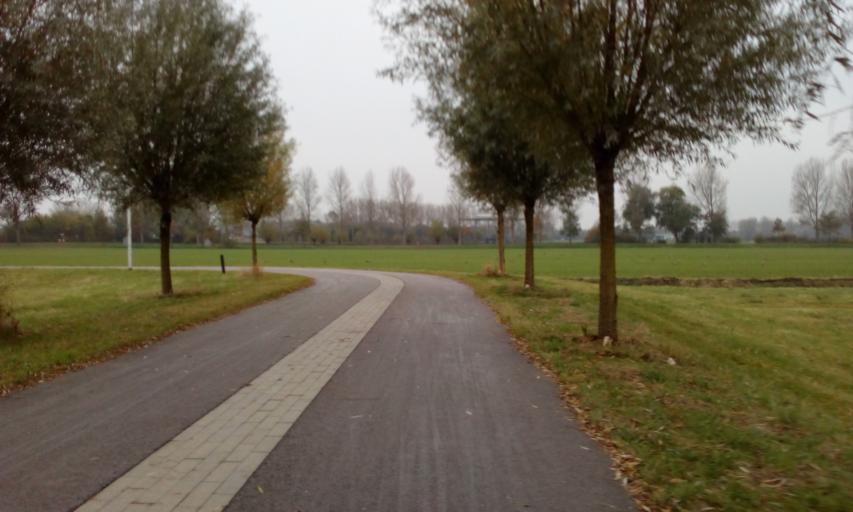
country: NL
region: South Holland
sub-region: Gemeente Lansingerland
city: Berkel en Rodenrijs
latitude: 51.9757
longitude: 4.4835
